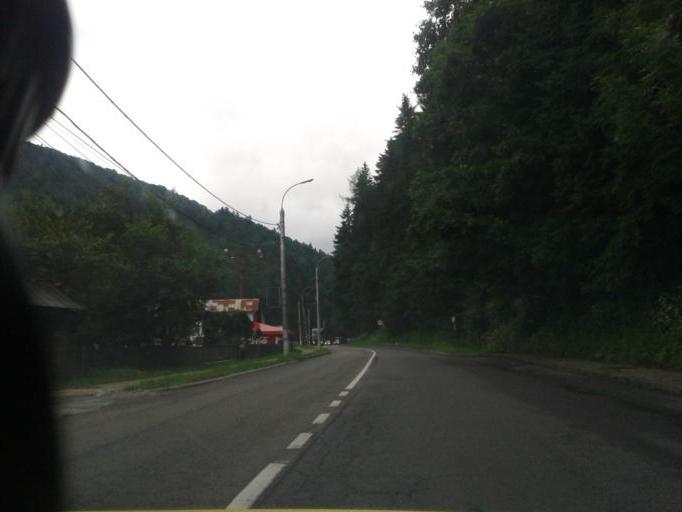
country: RO
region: Prahova
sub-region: Oras Azuga
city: Azuga
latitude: 45.4456
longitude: 25.5549
